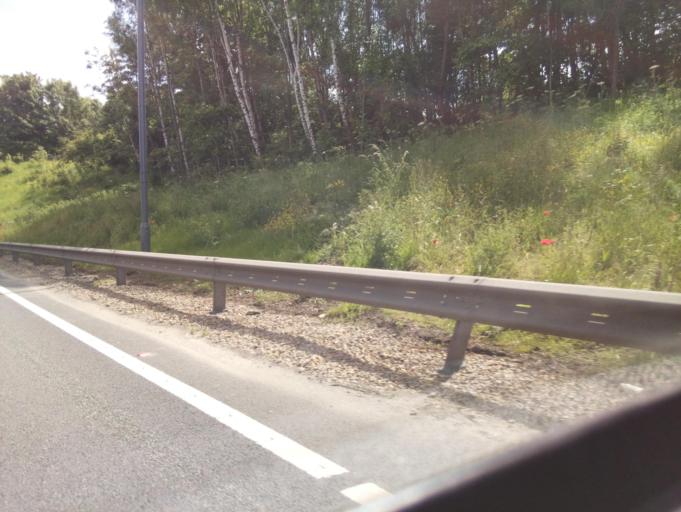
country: GB
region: England
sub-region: Stockton-on-Tees
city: Billingham
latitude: 54.6013
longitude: -1.3088
